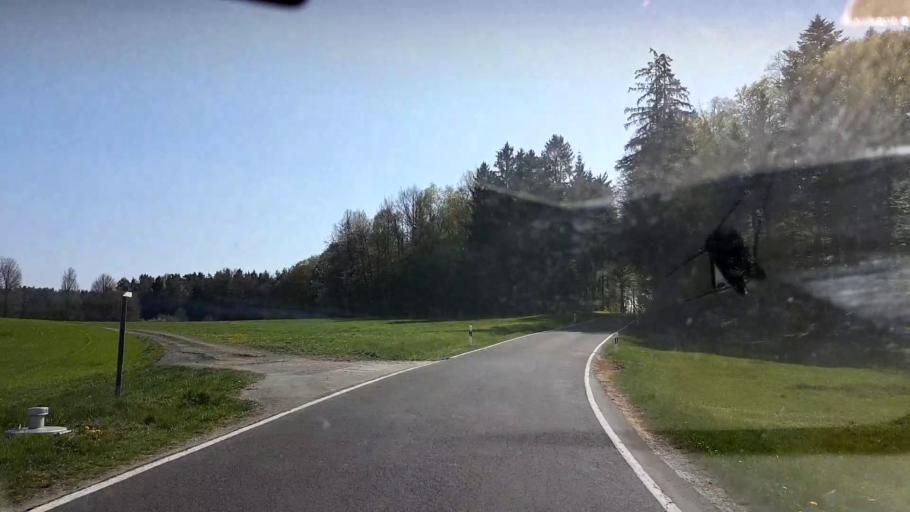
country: DE
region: Bavaria
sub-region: Upper Franconia
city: Pottenstein
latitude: 49.7970
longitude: 11.3984
